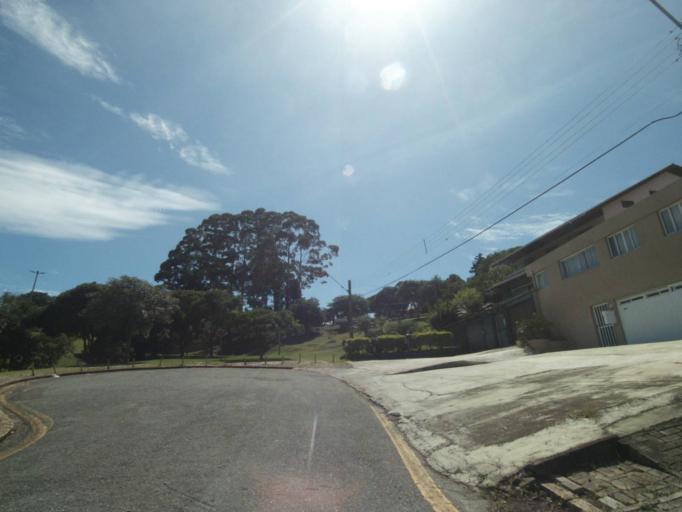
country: BR
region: Parana
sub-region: Curitiba
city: Curitiba
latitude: -25.4580
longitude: -49.2467
